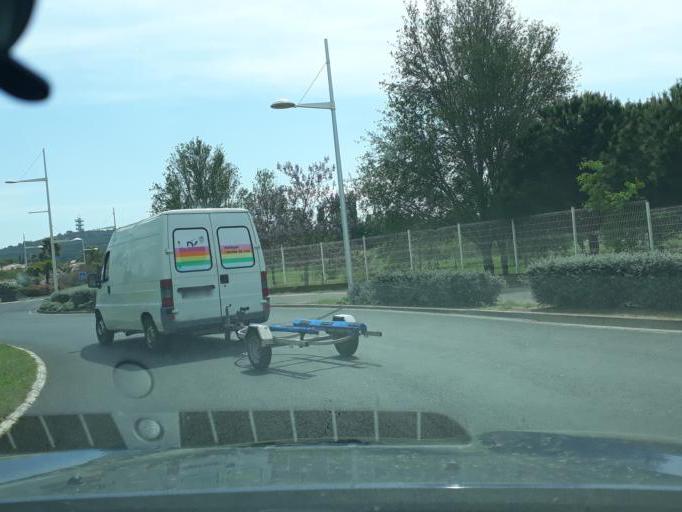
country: FR
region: Languedoc-Roussillon
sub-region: Departement de l'Herault
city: Agde
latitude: 43.3030
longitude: 3.4854
